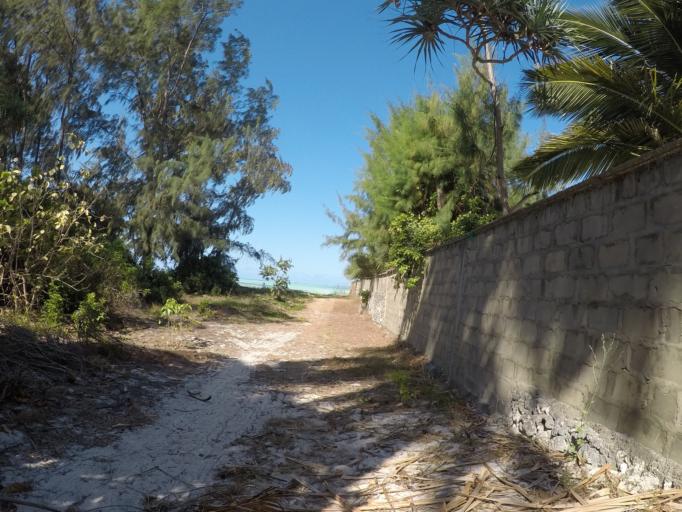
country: TZ
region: Zanzibar Central/South
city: Nganane
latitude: -6.2792
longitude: 39.5365
